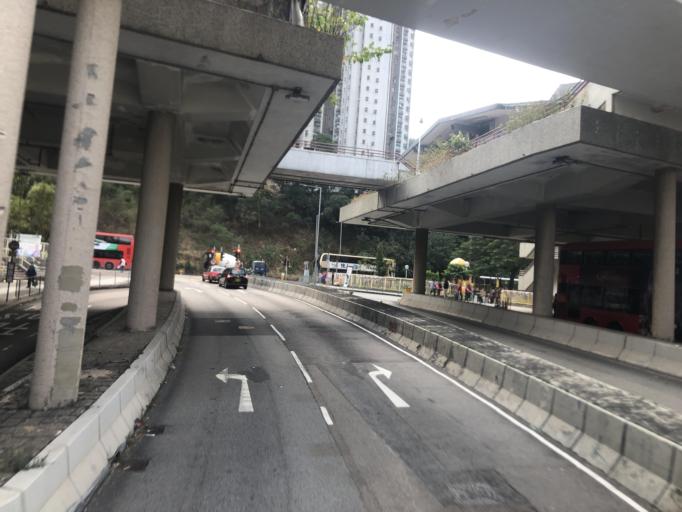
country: HK
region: Tsuen Wan
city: Tsuen Wan
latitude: 22.3502
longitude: 114.1007
